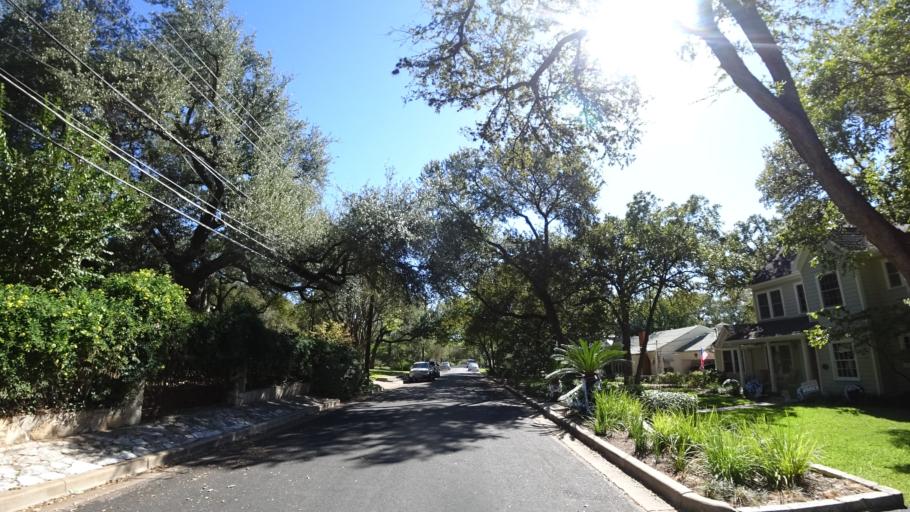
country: US
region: Texas
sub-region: Travis County
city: Rollingwood
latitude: 30.2897
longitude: -97.7676
